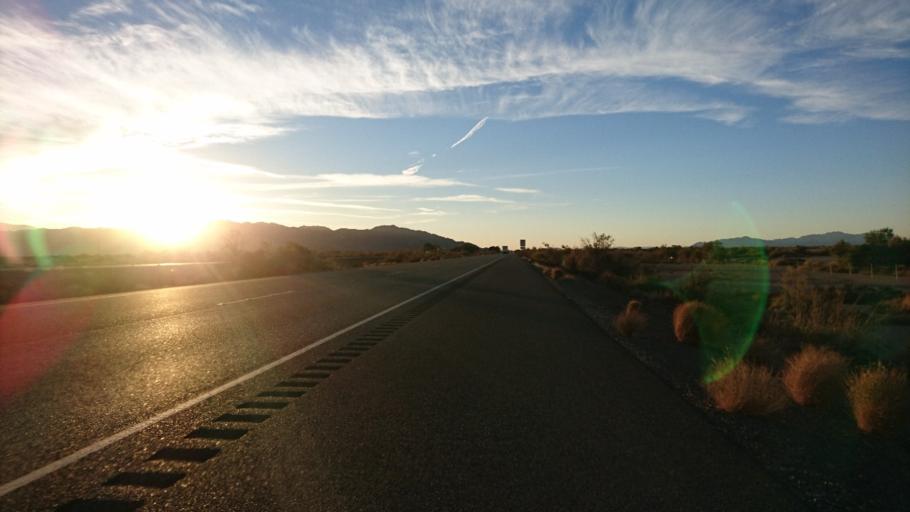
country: US
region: California
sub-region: San Bernardino County
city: Barstow
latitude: 34.8087
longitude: -116.5664
